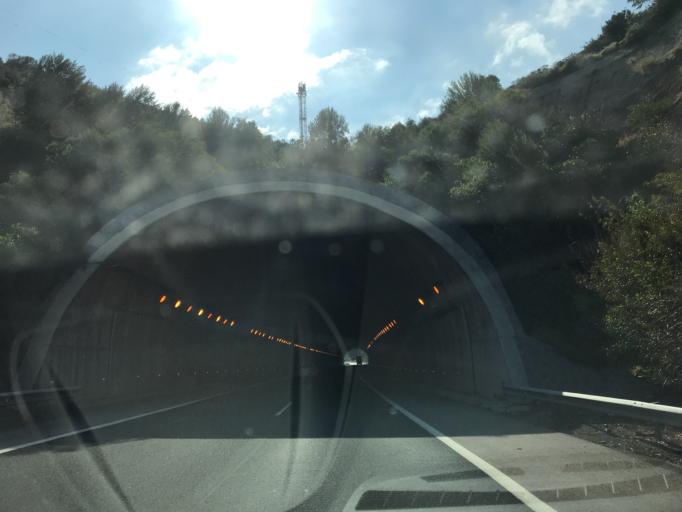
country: ES
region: Andalusia
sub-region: Provincia de Malaga
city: Istan
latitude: 36.5258
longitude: -4.9598
